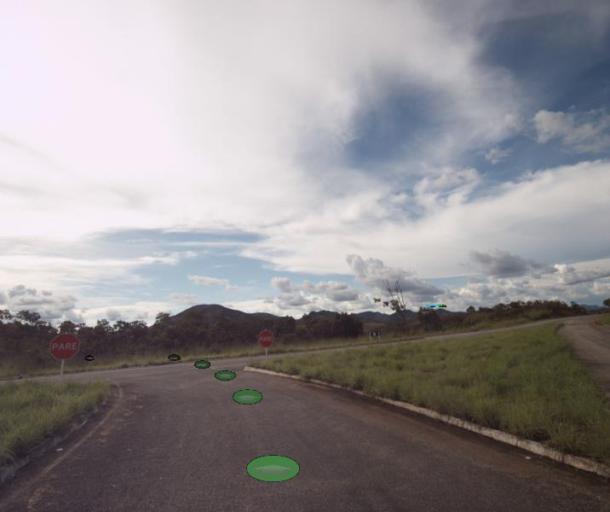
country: BR
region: Goias
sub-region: Barro Alto
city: Barro Alto
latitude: -15.1015
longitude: -48.7487
